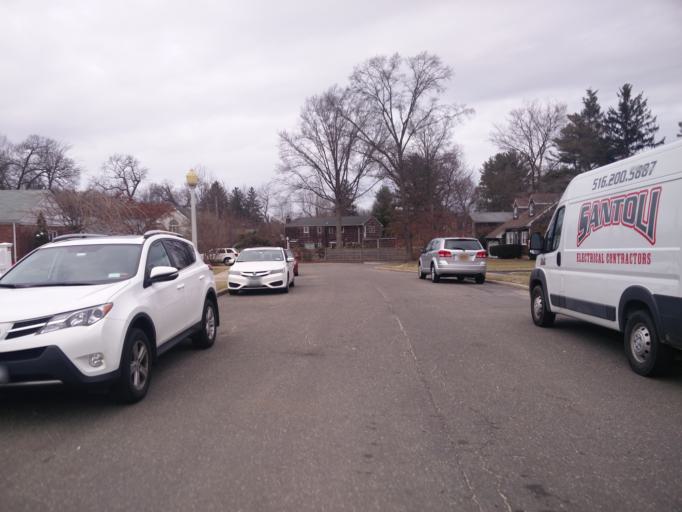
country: US
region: New York
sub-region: Nassau County
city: Glen Cove
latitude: 40.8763
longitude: -73.6286
